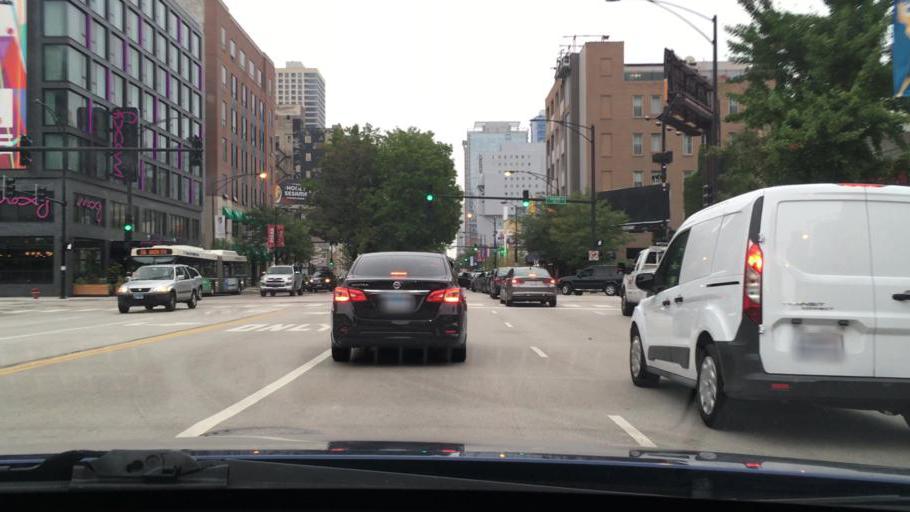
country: US
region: Illinois
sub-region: Cook County
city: Chicago
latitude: 41.8912
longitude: -87.6325
